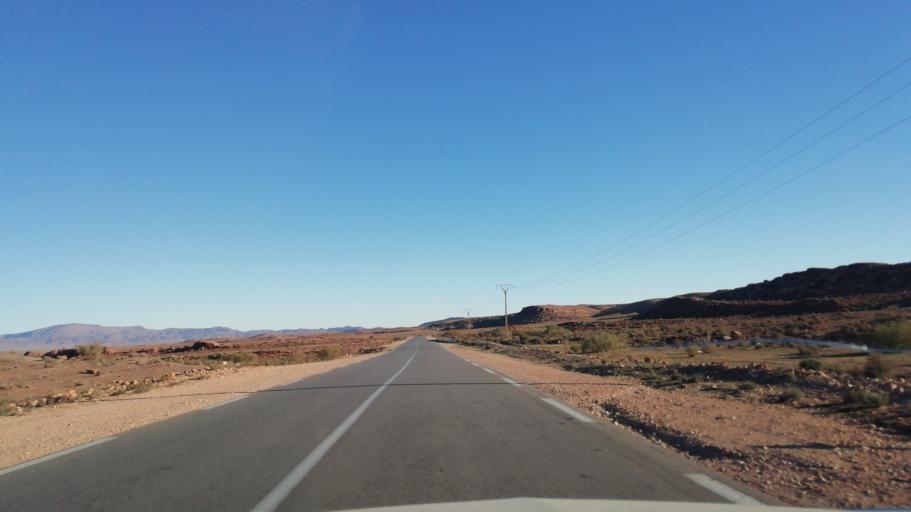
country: DZ
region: El Bayadh
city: El Abiodh Sidi Cheikh
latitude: 33.1714
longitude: 0.4569
